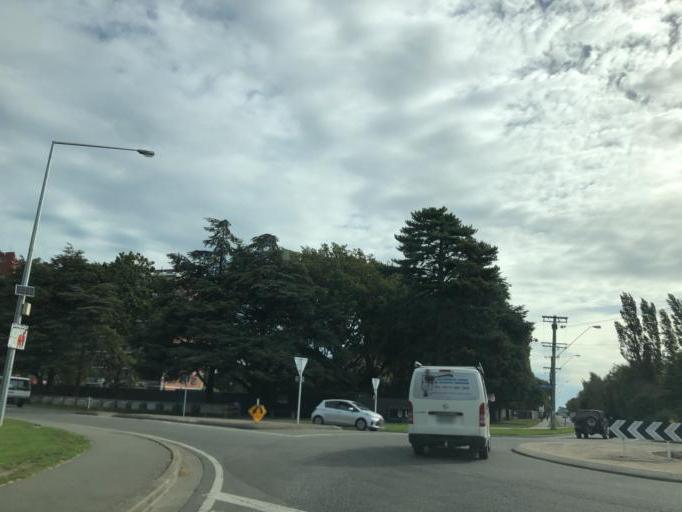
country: NZ
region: Canterbury
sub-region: Selwyn District
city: Lincoln
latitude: -43.6419
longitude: 172.4709
